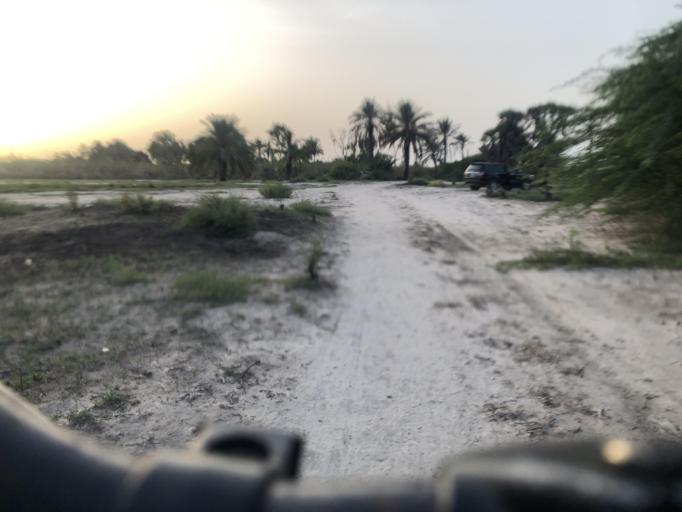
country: SN
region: Saint-Louis
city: Saint-Louis
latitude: 16.0724
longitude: -16.4313
